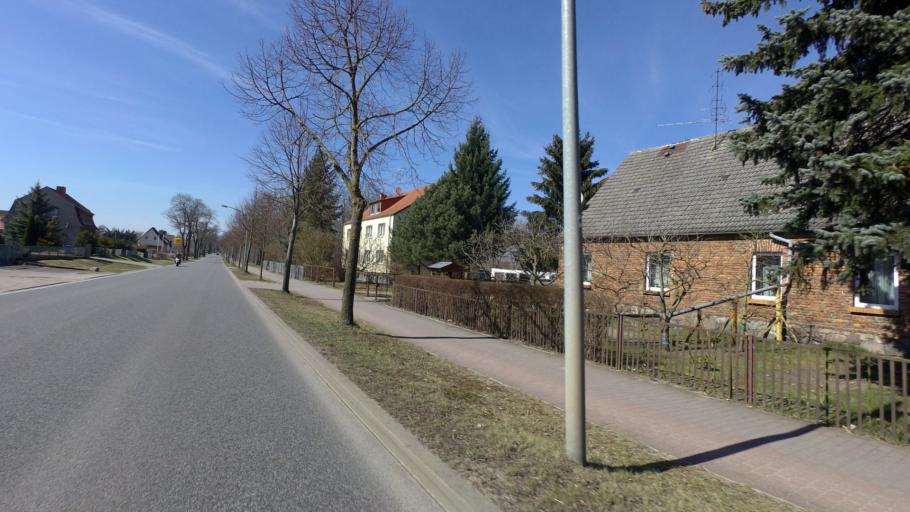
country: DE
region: Brandenburg
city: Muncheberg
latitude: 52.5096
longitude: 14.1261
